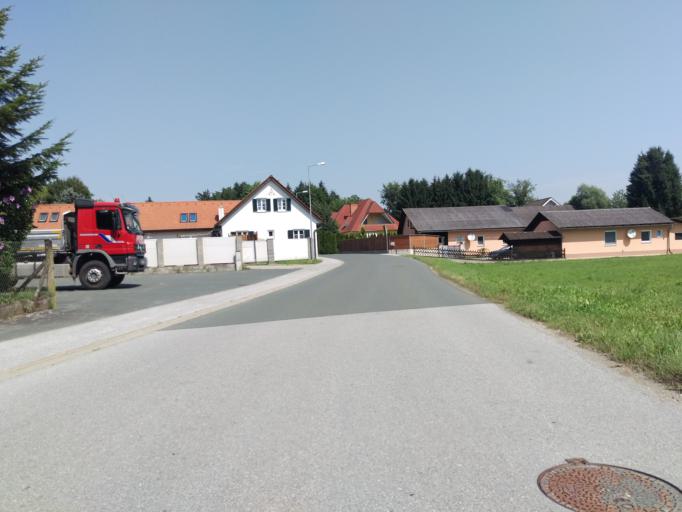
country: AT
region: Styria
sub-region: Politischer Bezirk Graz-Umgebung
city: Kalsdorf bei Graz
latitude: 46.9579
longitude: 15.4858
